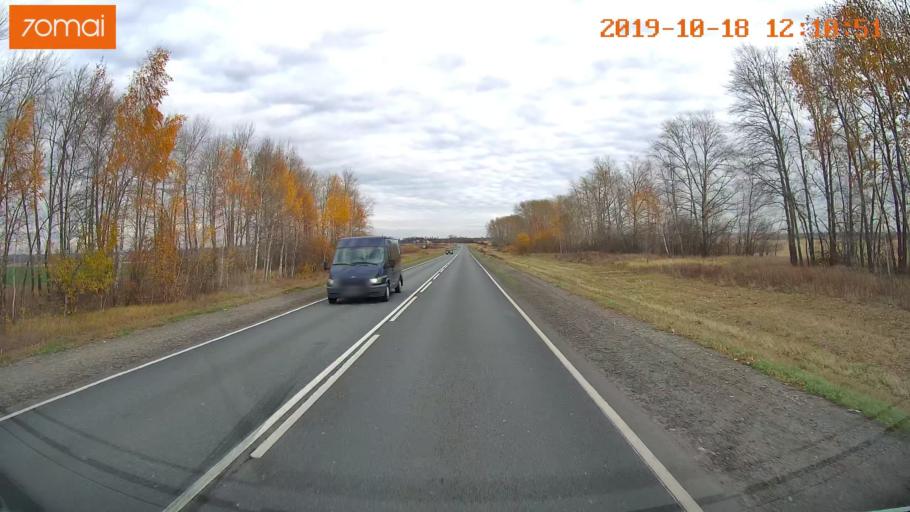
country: RU
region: Rjazan
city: Zakharovo
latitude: 54.3960
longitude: 39.3399
